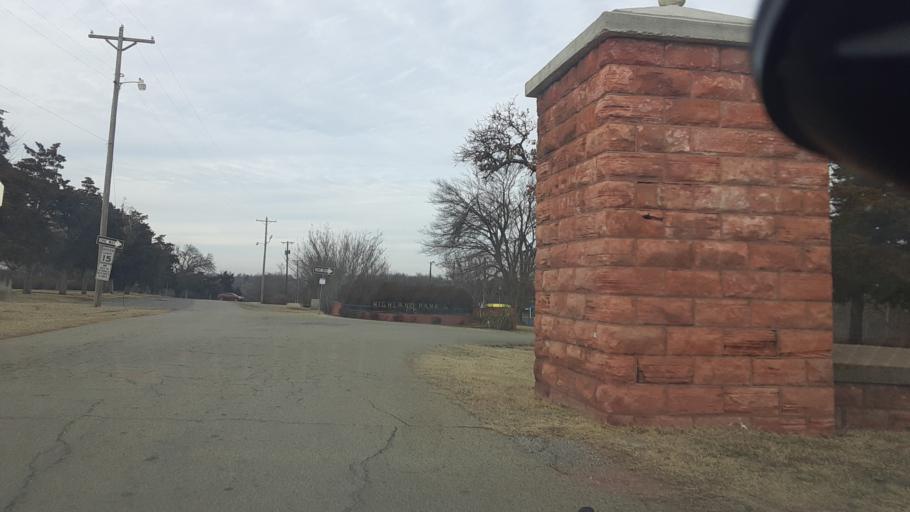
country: US
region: Oklahoma
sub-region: Logan County
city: Guthrie
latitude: 35.8813
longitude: -97.4124
